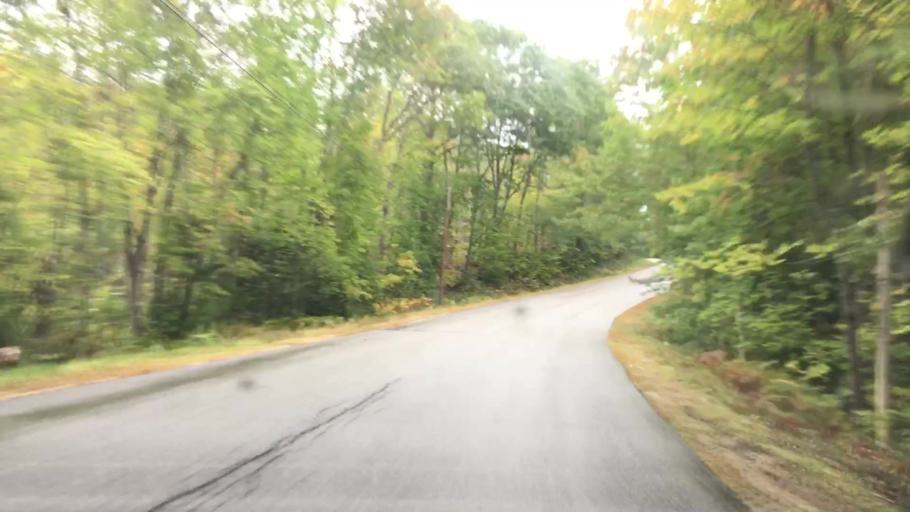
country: US
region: Maine
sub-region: Cumberland County
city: Harrison
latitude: 44.0521
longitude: -70.6181
